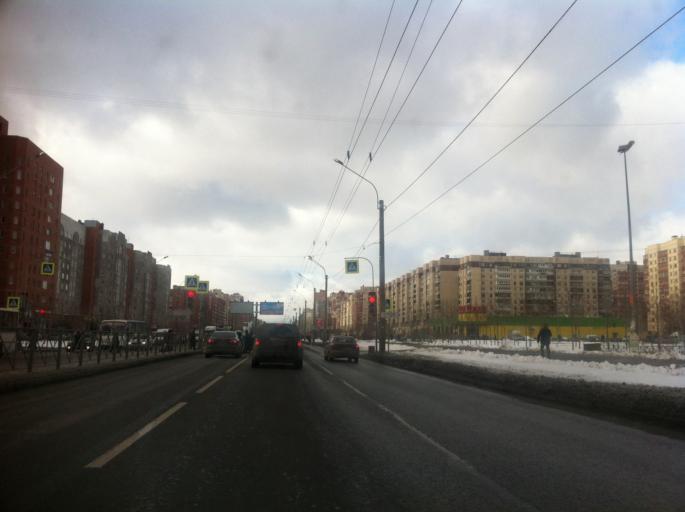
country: RU
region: St.-Petersburg
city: Dachnoye
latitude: 59.8527
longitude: 30.2181
